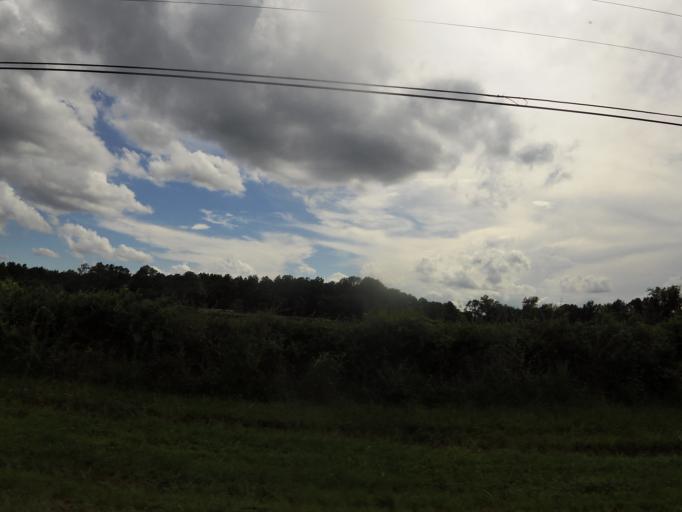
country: US
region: Florida
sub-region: Clay County
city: Asbury Lake
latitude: 30.0719
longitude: -81.7739
